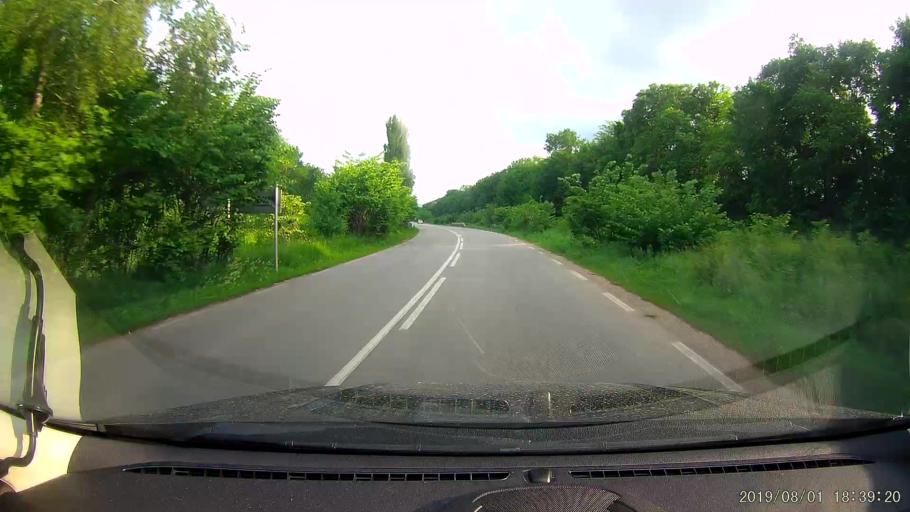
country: BG
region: Shumen
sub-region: Obshtina Khitrino
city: Gara Khitrino
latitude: 43.3878
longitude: 26.9168
